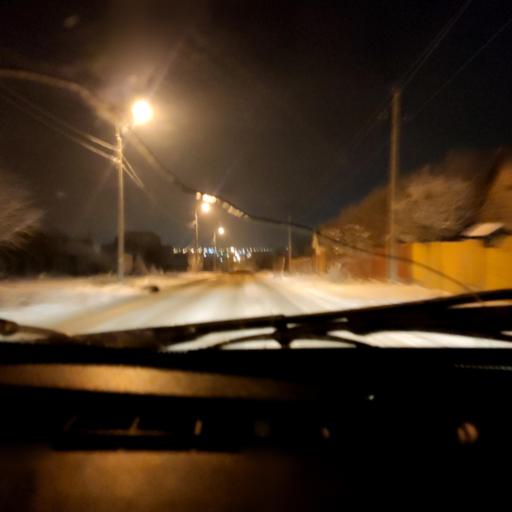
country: RU
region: Bashkortostan
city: Ufa
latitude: 54.6006
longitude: 55.9510
